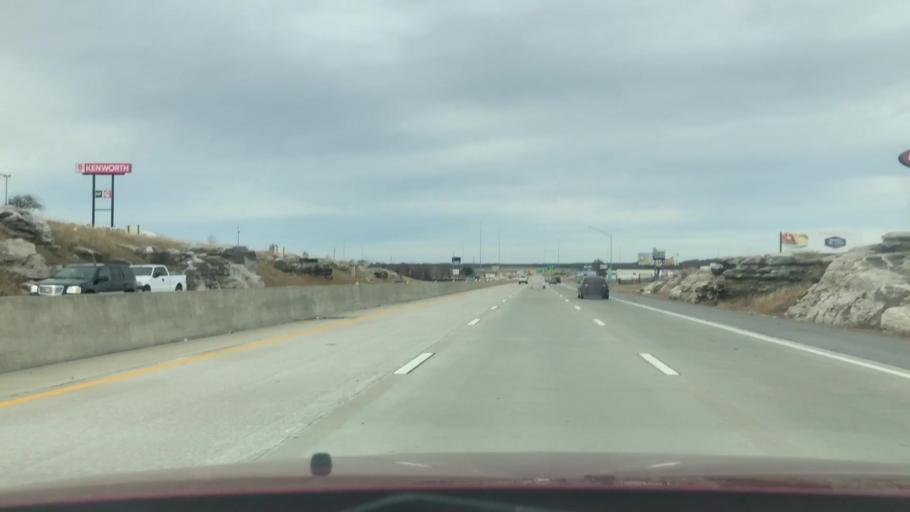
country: US
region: Missouri
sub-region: Greene County
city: Springfield
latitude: 37.2394
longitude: -93.2246
